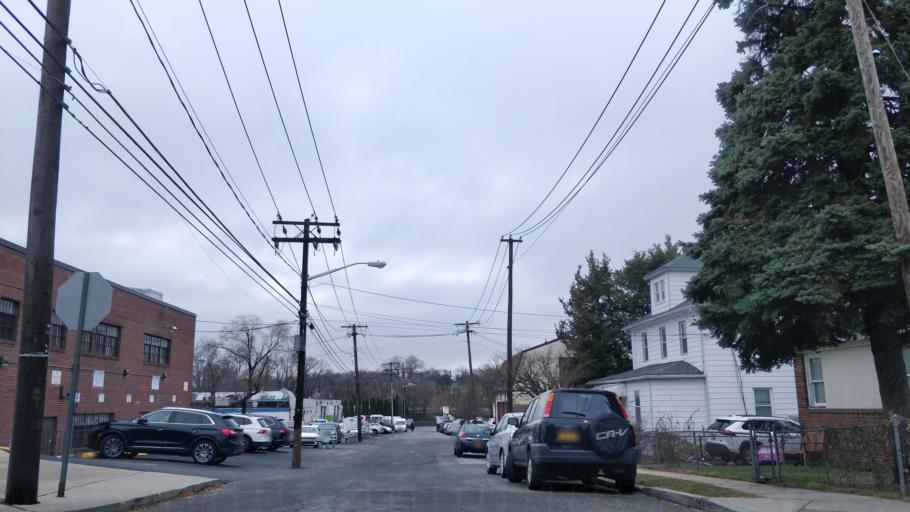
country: US
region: New York
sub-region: Nassau County
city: Glen Cove
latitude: 40.8545
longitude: -73.6212
